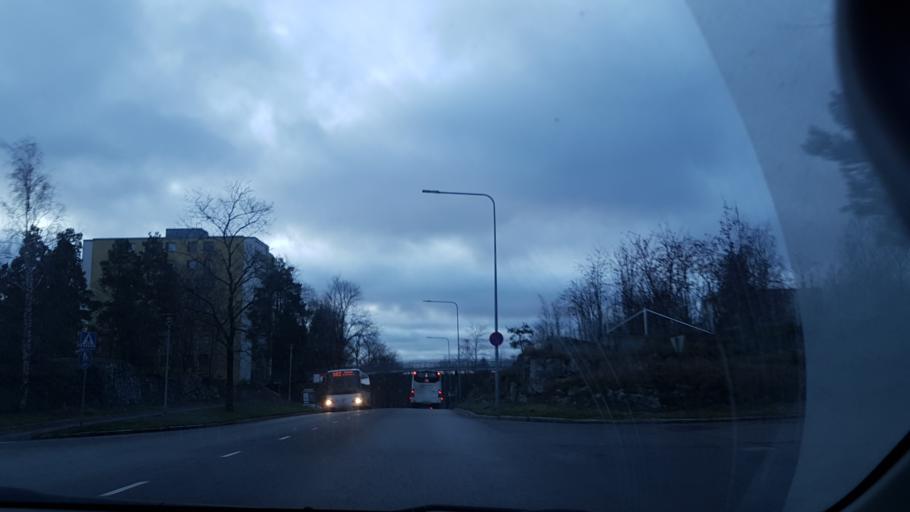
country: FI
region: Uusimaa
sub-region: Helsinki
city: Vantaa
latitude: 60.2737
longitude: 25.1041
